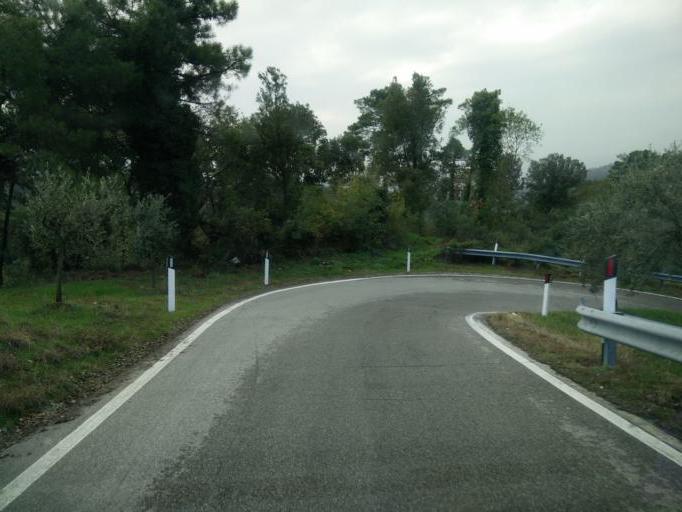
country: IT
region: Tuscany
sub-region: Provincia di Prato
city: Vaiano
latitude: 43.9362
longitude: 11.0962
